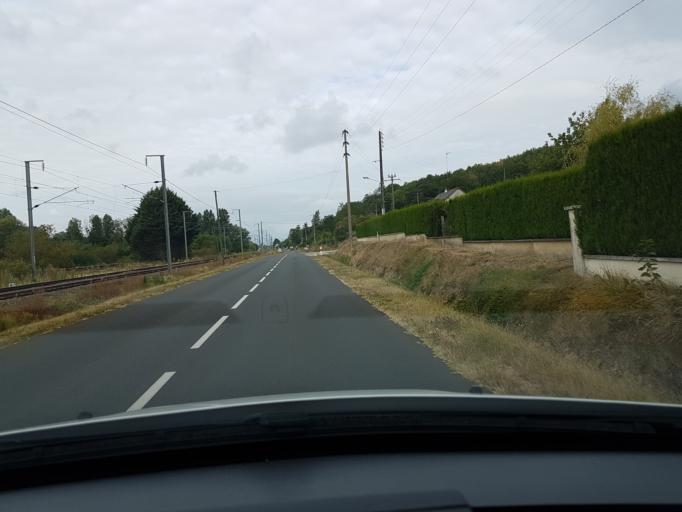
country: FR
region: Centre
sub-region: Departement d'Indre-et-Loire
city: Saint-Martin-le-Beau
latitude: 47.3491
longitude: 0.9375
